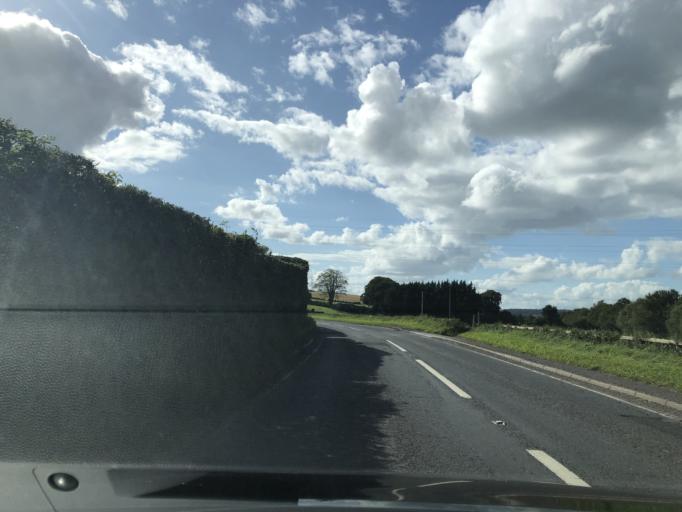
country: GB
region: Northern Ireland
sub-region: Castlereagh District
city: Dundonald
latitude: 54.5703
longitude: -5.7735
